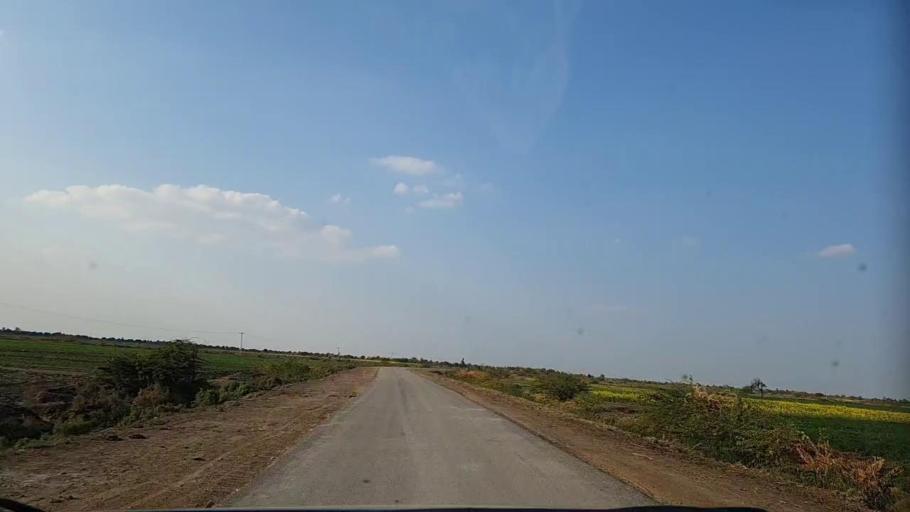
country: PK
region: Sindh
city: Pithoro
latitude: 25.7148
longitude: 69.2197
